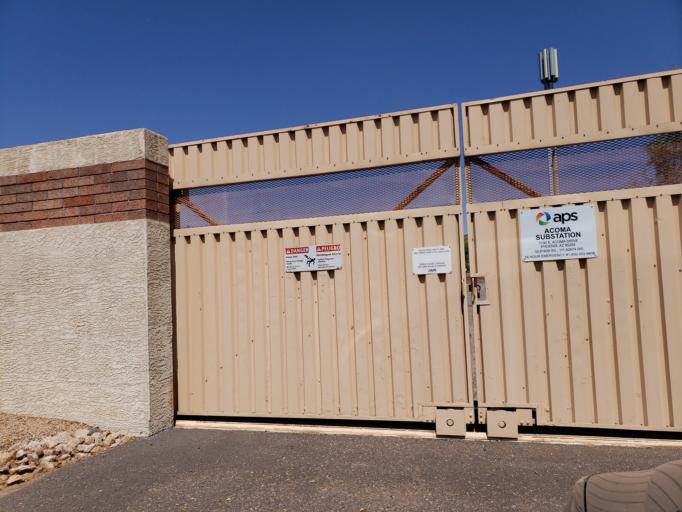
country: US
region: Arizona
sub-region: Maricopa County
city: Paradise Valley
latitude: 33.6180
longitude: -111.9275
